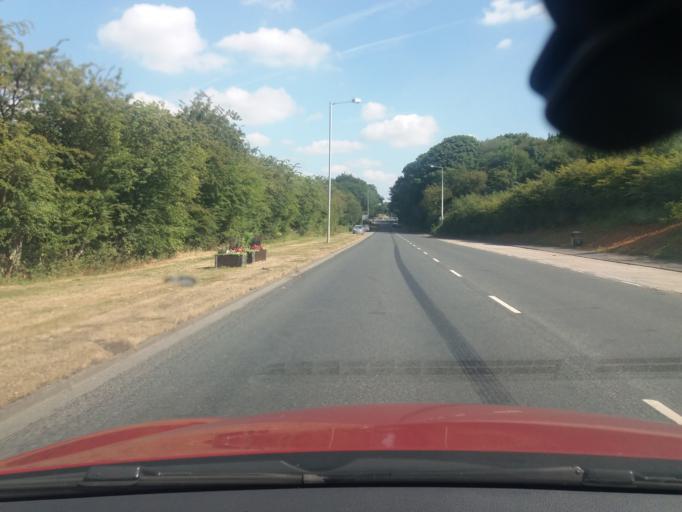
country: GB
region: England
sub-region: Lancashire
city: Adlington
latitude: 53.6254
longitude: -2.6109
